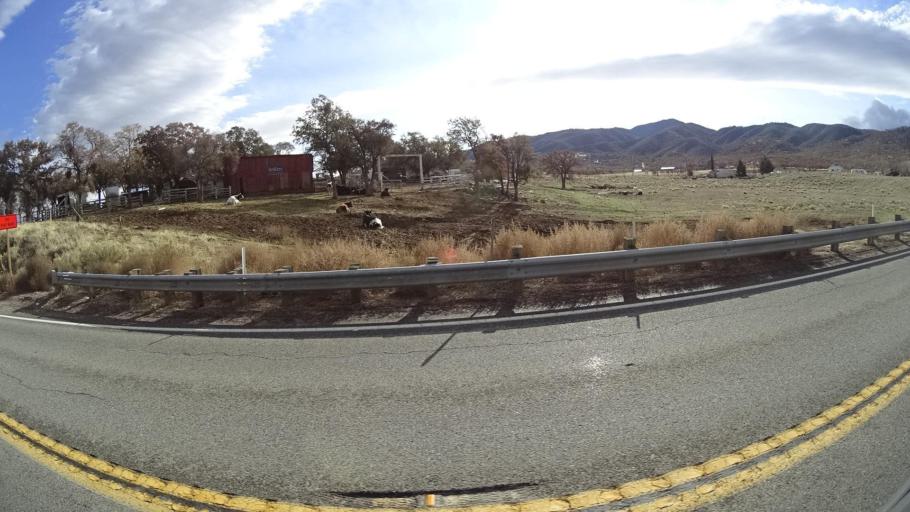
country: US
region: California
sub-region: Kern County
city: Golden Hills
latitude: 35.1130
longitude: -118.5094
